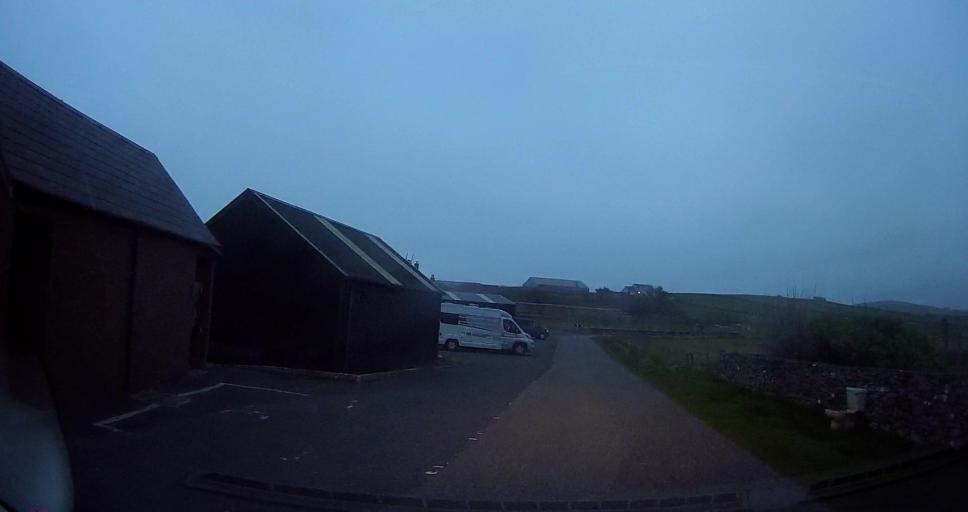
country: GB
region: Scotland
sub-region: Shetland Islands
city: Sandwick
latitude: 60.0067
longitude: -1.2222
